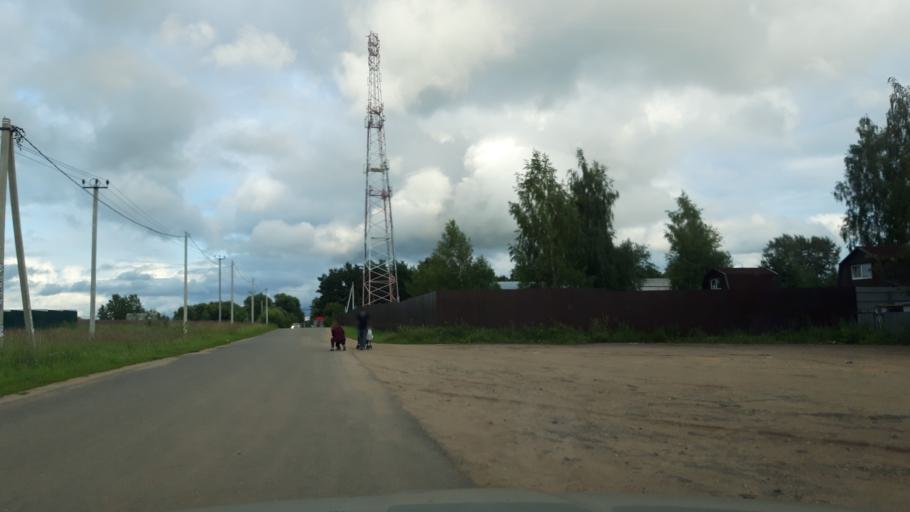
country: RU
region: Moskovskaya
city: Istra
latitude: 56.0951
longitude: 36.7970
